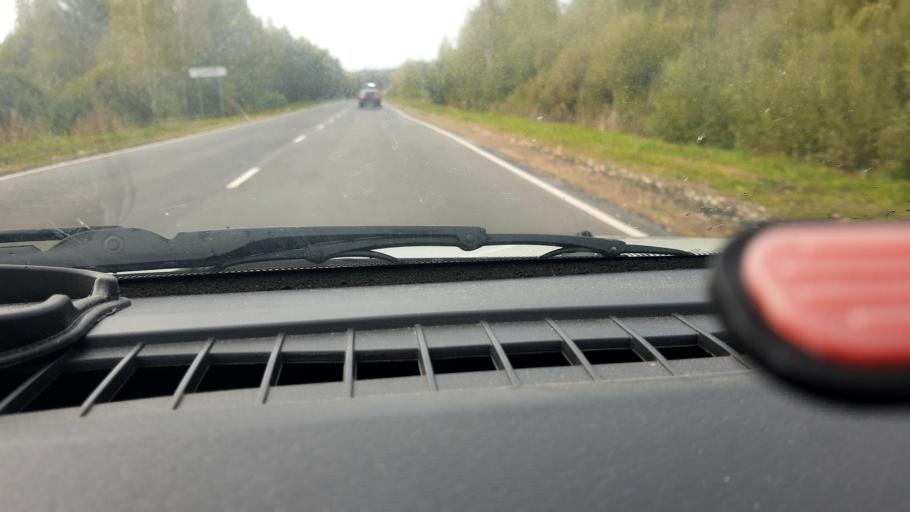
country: RU
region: Nizjnij Novgorod
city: Prudy
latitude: 57.3517
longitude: 46.2307
